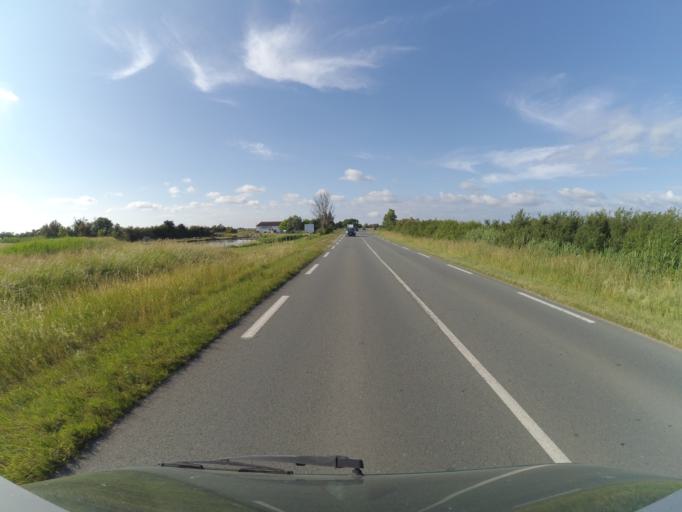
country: FR
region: Poitou-Charentes
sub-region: Departement de la Charente-Maritime
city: Le Gua
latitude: 45.7125
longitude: -0.9728
